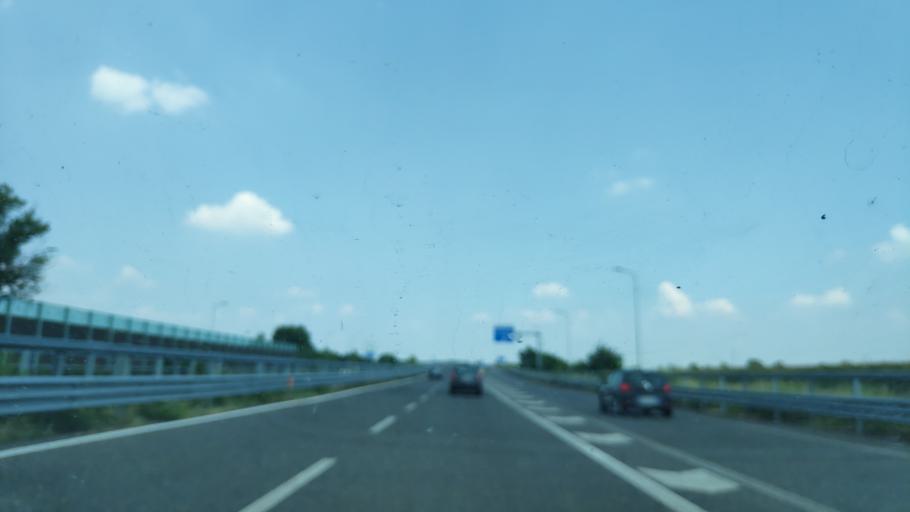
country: IT
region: Lombardy
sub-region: Citta metropolitana di Milano
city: Millepini
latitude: 45.4797
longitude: 9.3270
